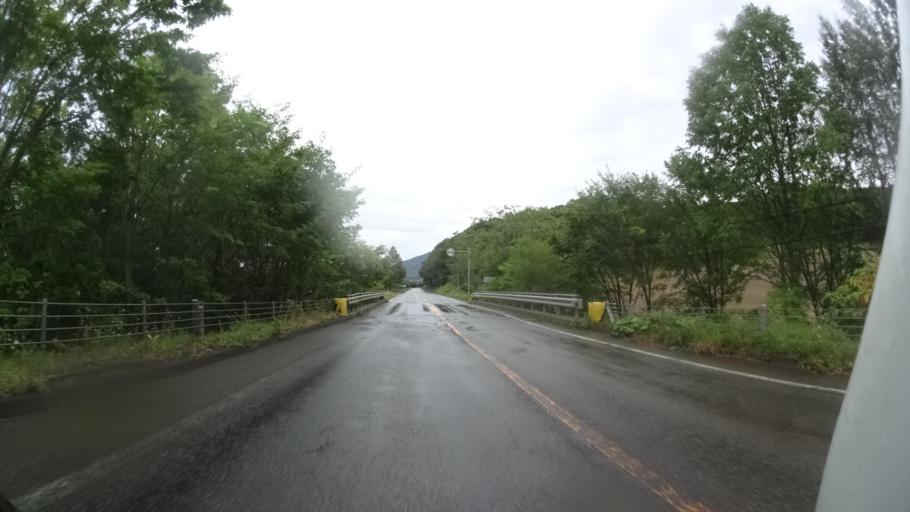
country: JP
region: Hokkaido
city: Kitami
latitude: 44.0966
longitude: 143.7818
